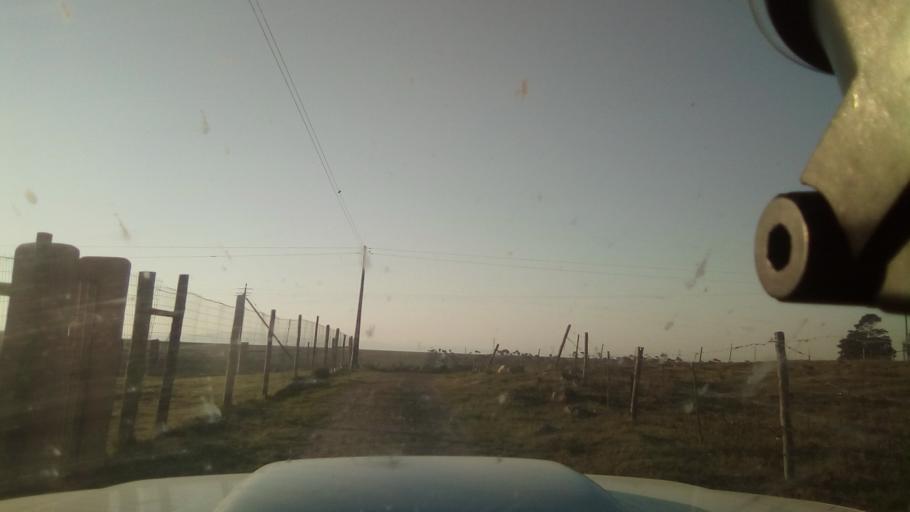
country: ZA
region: Eastern Cape
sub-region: Buffalo City Metropolitan Municipality
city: Bhisho
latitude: -32.9728
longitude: 27.2935
